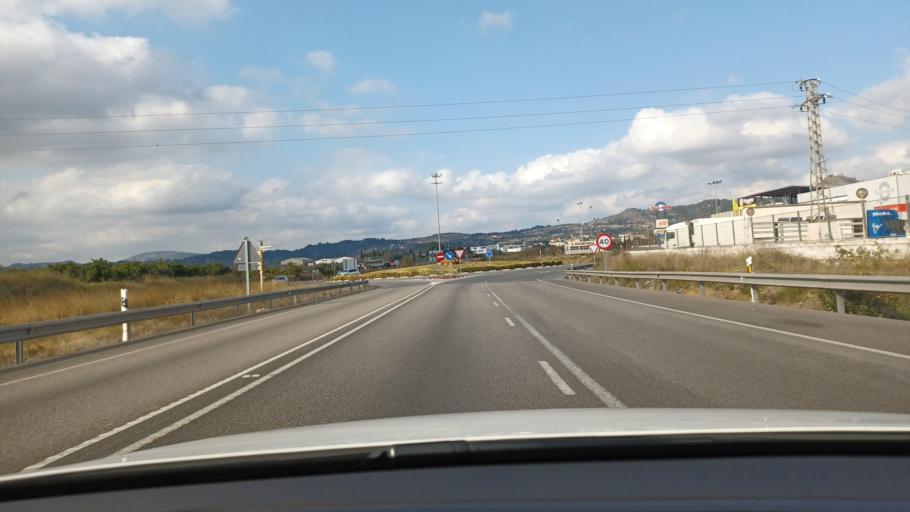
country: ES
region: Valencia
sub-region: Provincia de Valencia
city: Xativa
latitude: 39.0010
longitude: -0.5281
